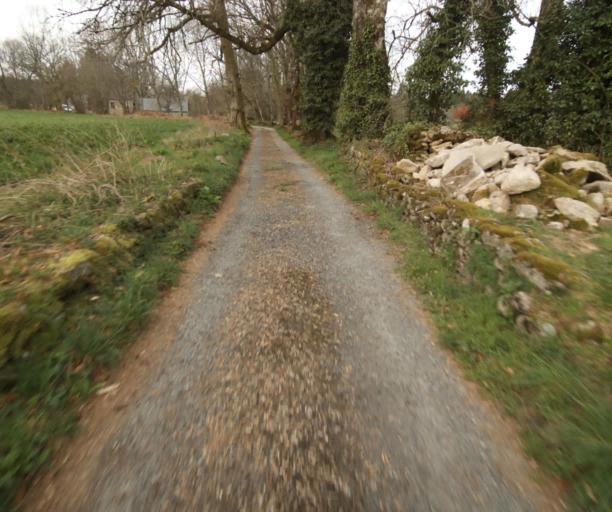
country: FR
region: Limousin
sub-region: Departement de la Correze
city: Correze
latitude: 45.4234
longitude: 1.8374
